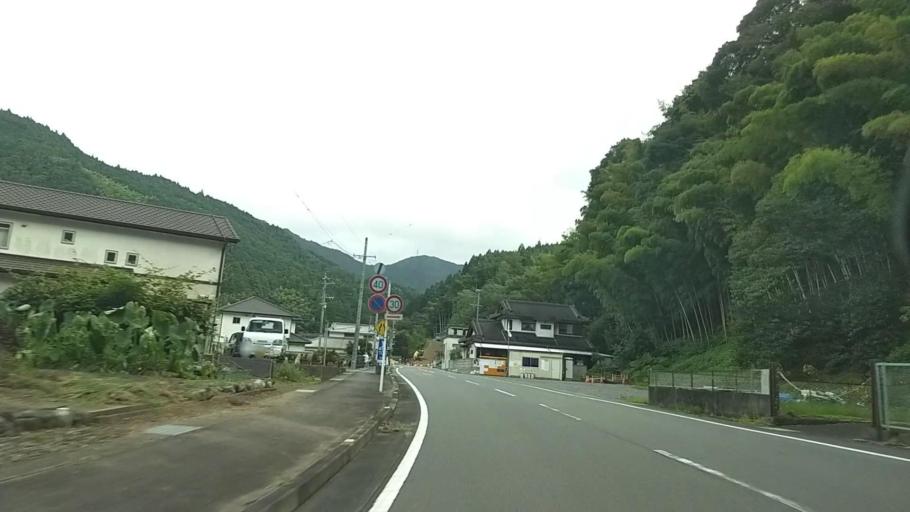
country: JP
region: Shizuoka
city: Fujinomiya
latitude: 35.1694
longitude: 138.5387
